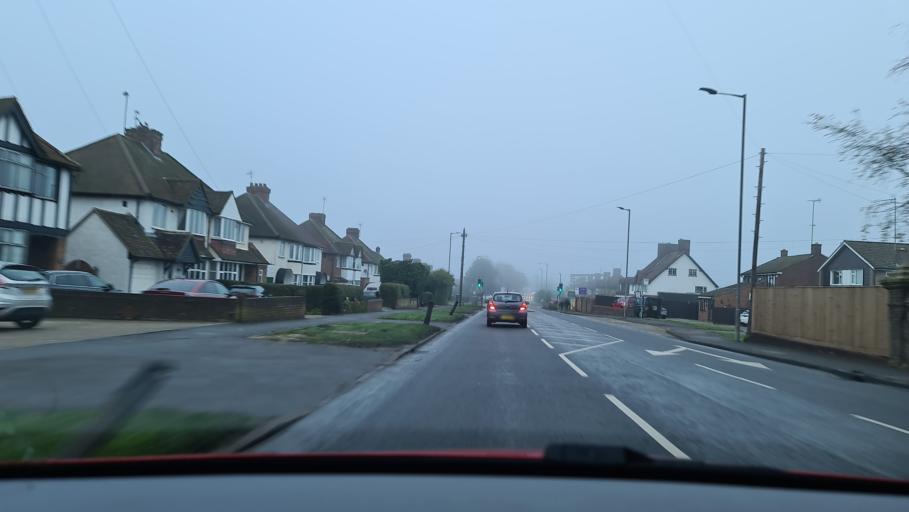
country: GB
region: England
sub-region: Buckinghamshire
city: Aylesbury
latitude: 51.8131
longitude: -0.7829
